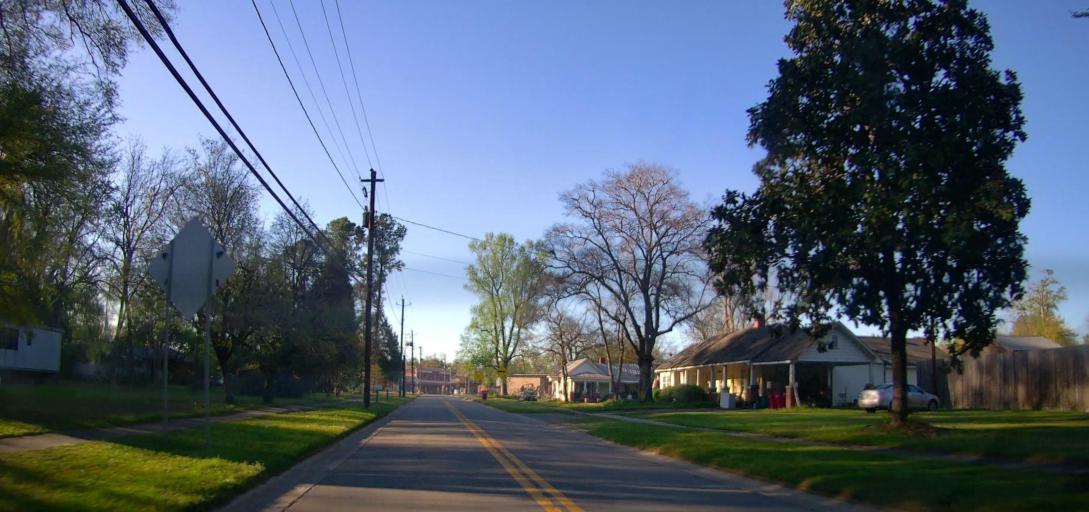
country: US
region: Georgia
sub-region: Wilkinson County
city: Irwinton
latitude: 32.8244
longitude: -83.0793
